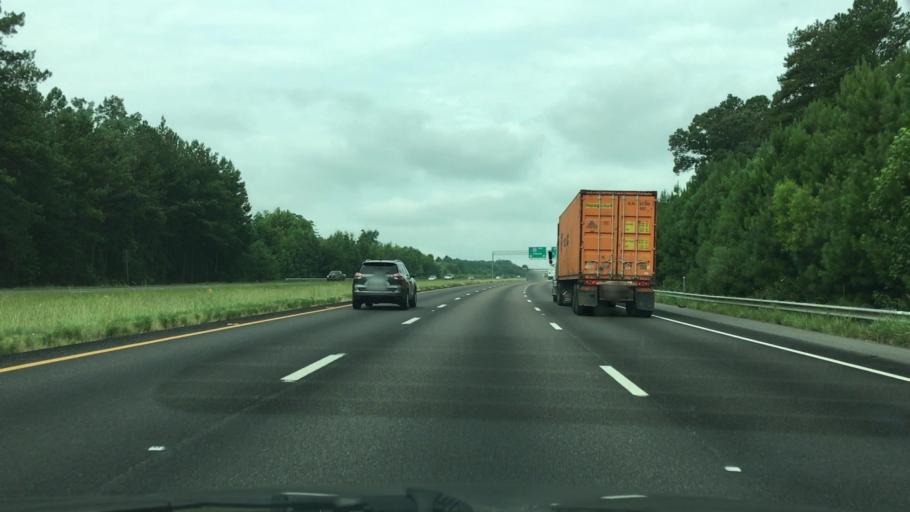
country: US
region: South Carolina
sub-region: Edgefield County
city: Murphys Estates
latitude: 33.5705
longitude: -81.9160
